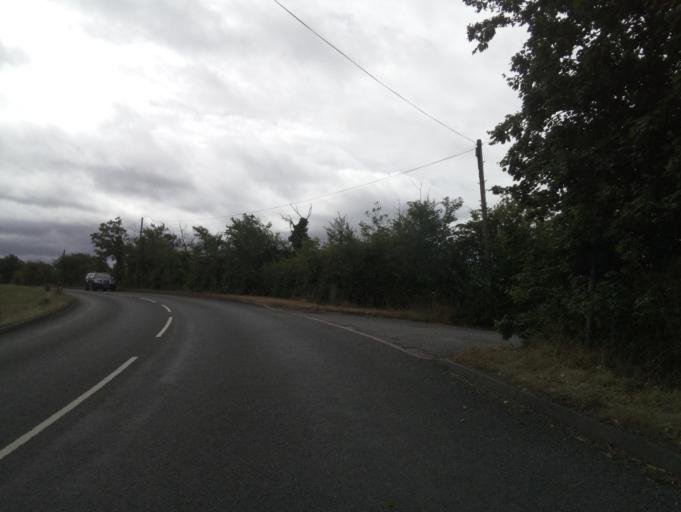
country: GB
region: England
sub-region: Derbyshire
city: Long Eaton
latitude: 52.9233
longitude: -1.3102
